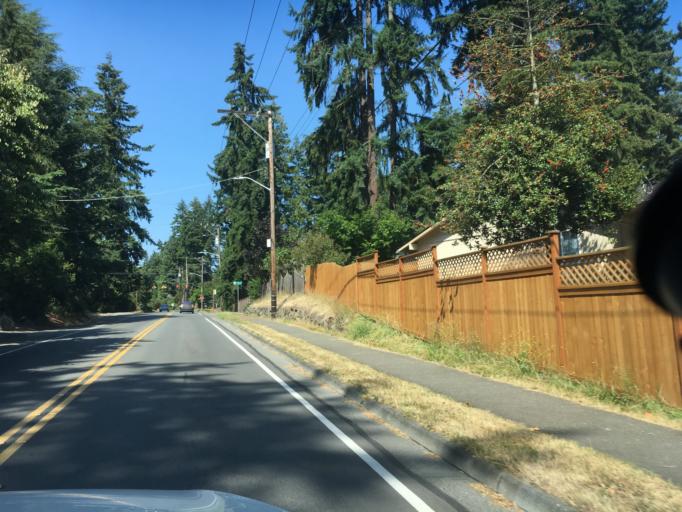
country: US
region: Washington
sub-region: King County
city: Shoreline
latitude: 47.7529
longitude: -122.3537
